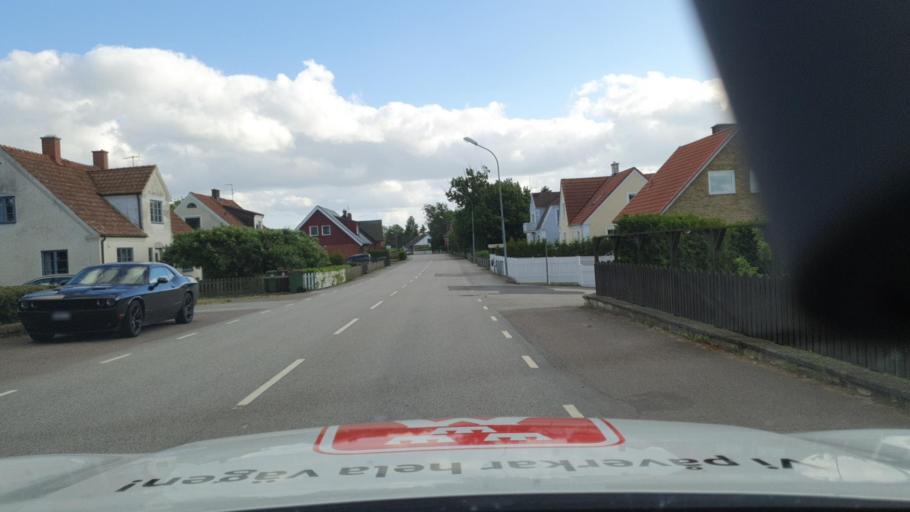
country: SE
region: Skane
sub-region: Tomelilla Kommun
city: Tomelilla
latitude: 55.5837
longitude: 14.0165
